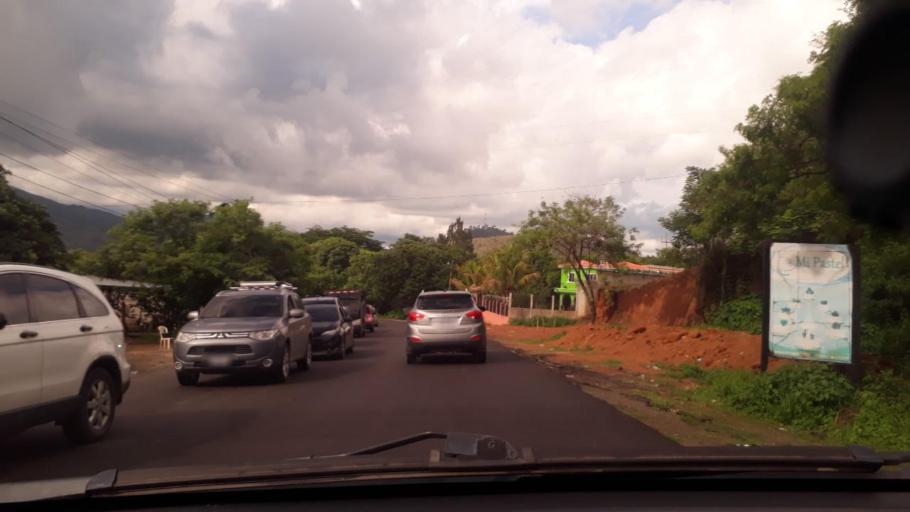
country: GT
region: Jutiapa
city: Quesada
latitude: 14.2651
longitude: -90.0111
